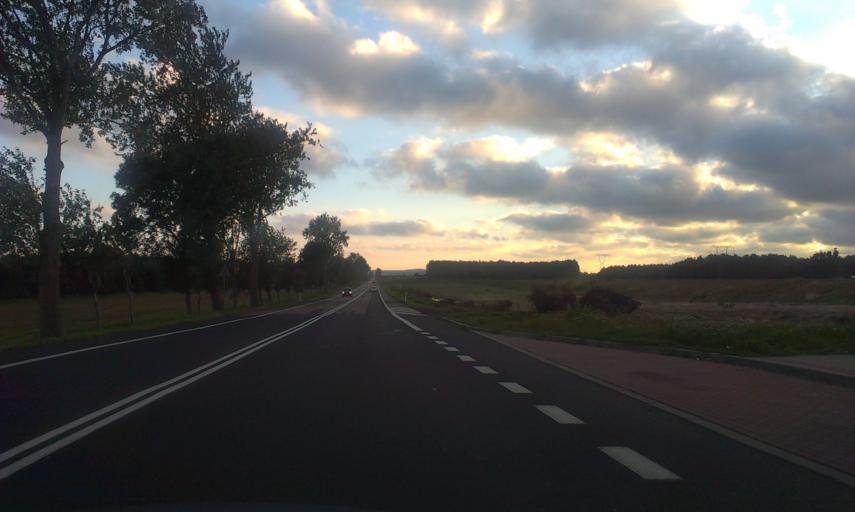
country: PL
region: West Pomeranian Voivodeship
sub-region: Powiat koszalinski
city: Sianow
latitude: 54.2488
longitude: 16.3511
